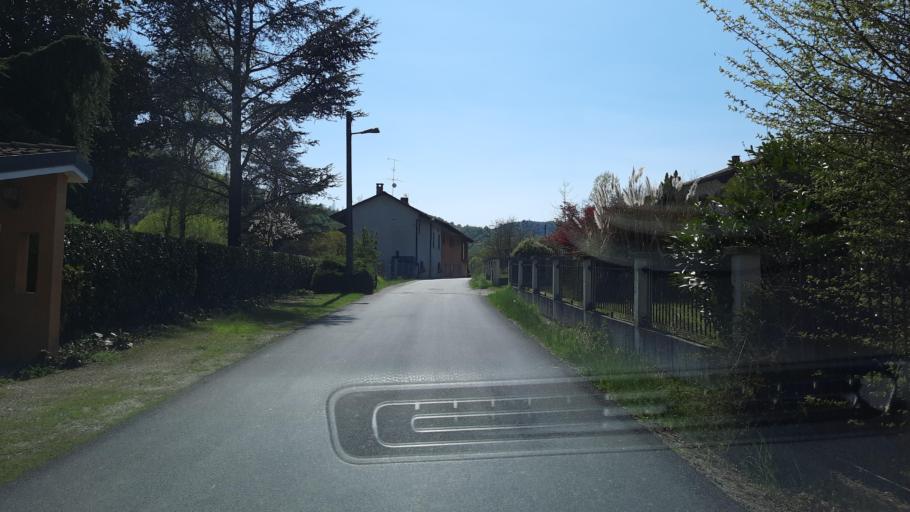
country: IT
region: Piedmont
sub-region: Provincia di Torino
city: Valentino
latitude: 45.1376
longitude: 8.1226
